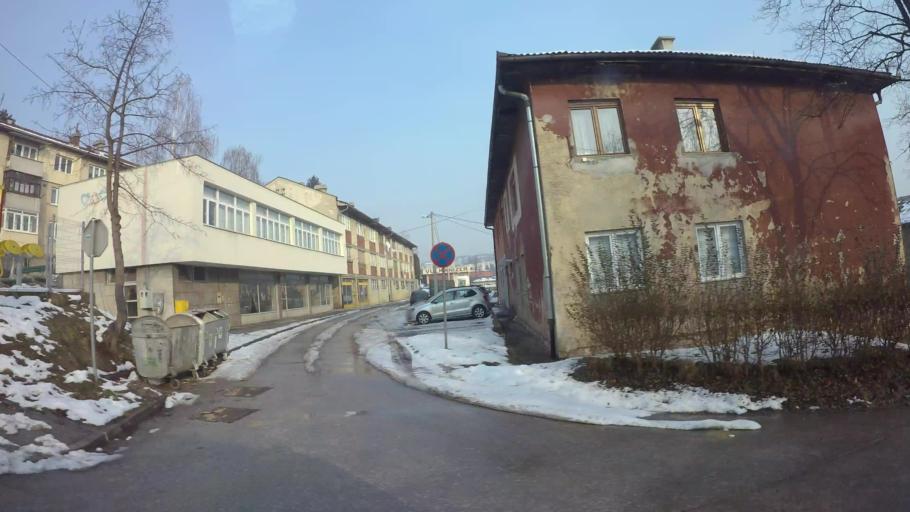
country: BA
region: Federation of Bosnia and Herzegovina
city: Kobilja Glava
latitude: 43.8659
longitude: 18.3986
